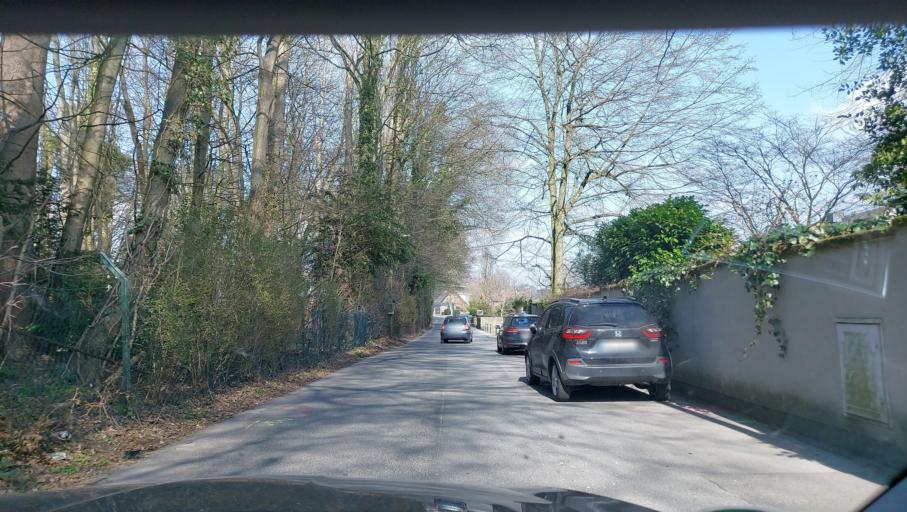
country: DE
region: North Rhine-Westphalia
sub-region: Regierungsbezirk Dusseldorf
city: Erkrath
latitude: 51.2551
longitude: 6.8772
